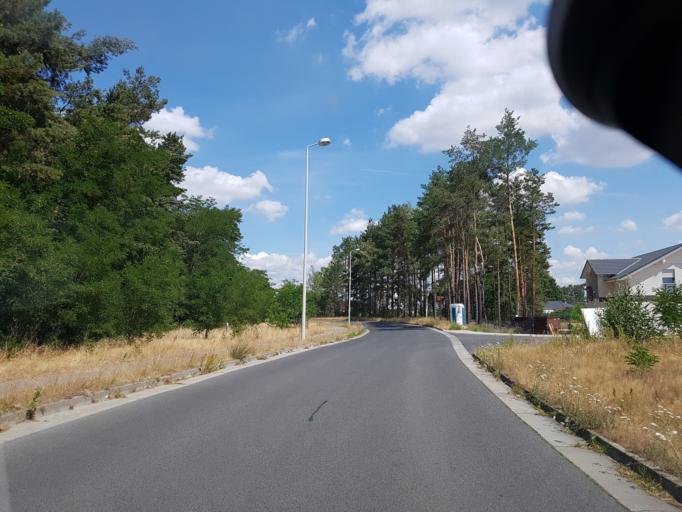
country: DE
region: Brandenburg
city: Cottbus
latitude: 51.7076
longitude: 14.3461
